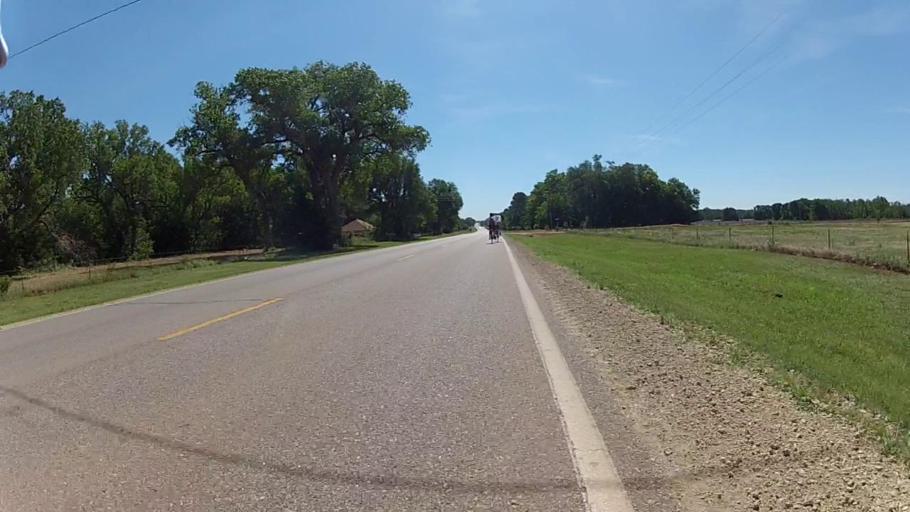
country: US
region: Kansas
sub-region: Barber County
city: Medicine Lodge
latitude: 37.2752
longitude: -98.6058
